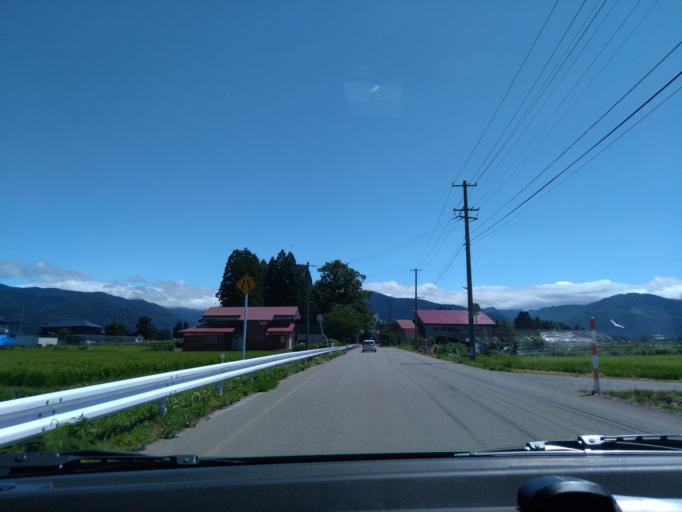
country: JP
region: Akita
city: Kakunodatemachi
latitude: 39.5298
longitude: 140.6006
